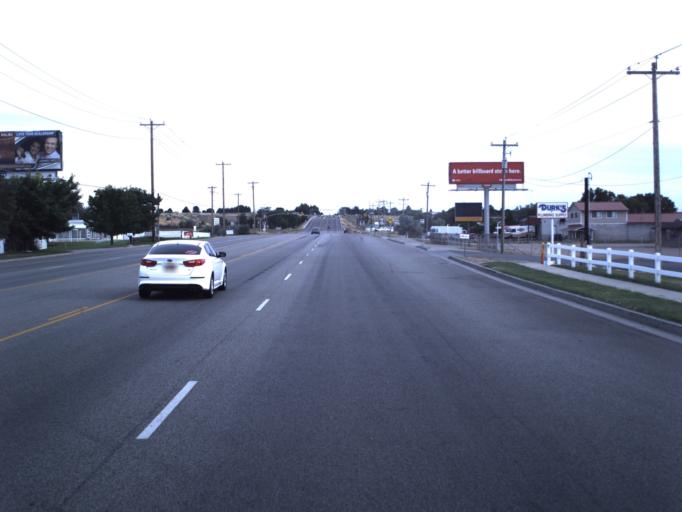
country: US
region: Utah
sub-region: Weber County
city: West Haven
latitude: 41.2084
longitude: -112.0259
